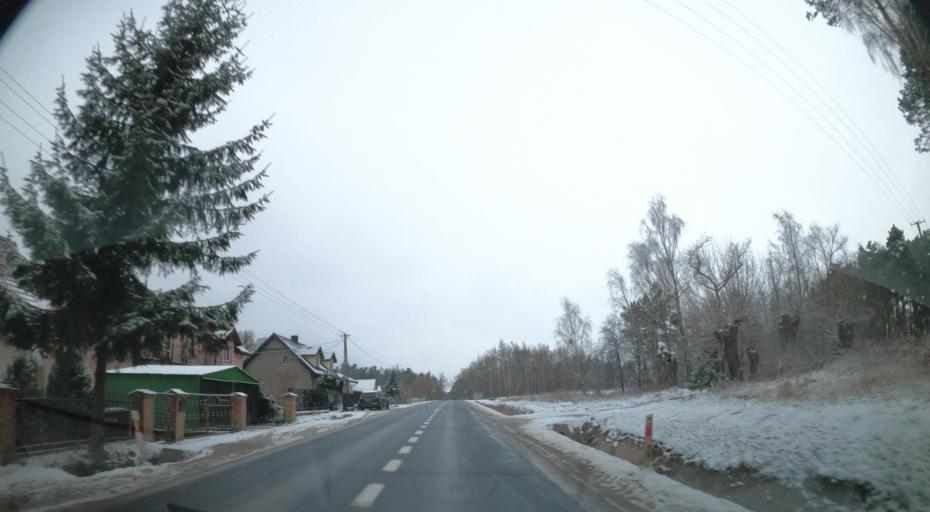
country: PL
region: Masovian Voivodeship
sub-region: Powiat plocki
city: Nowy Duninow
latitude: 52.6101
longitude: 19.4728
